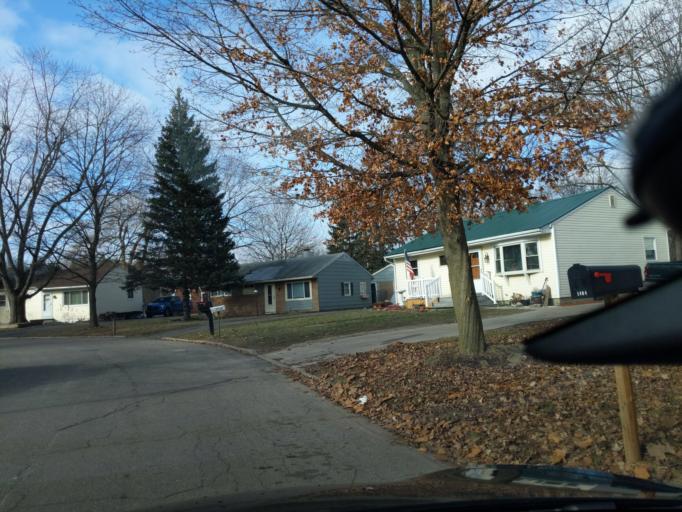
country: US
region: Michigan
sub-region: Ingham County
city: Lansing
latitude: 42.6954
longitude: -84.5714
